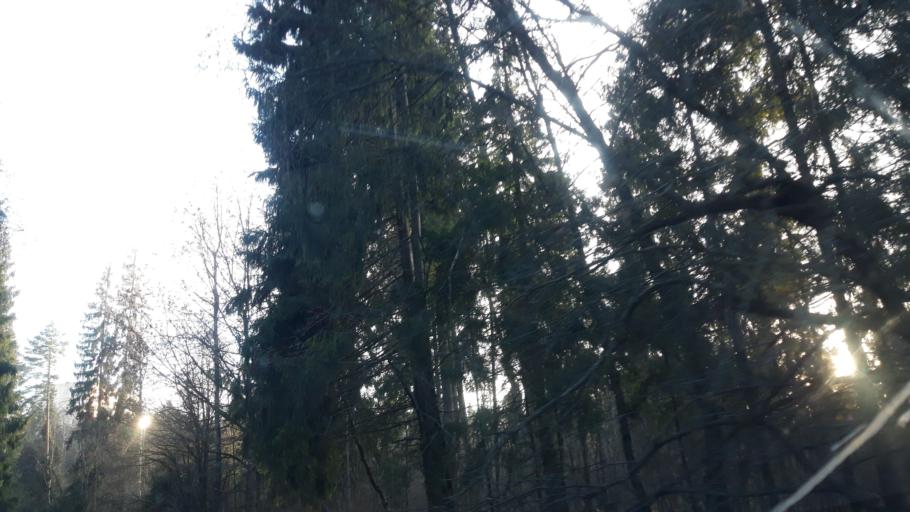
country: RU
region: Moskovskaya
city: Rzhavki
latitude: 56.0010
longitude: 37.2269
